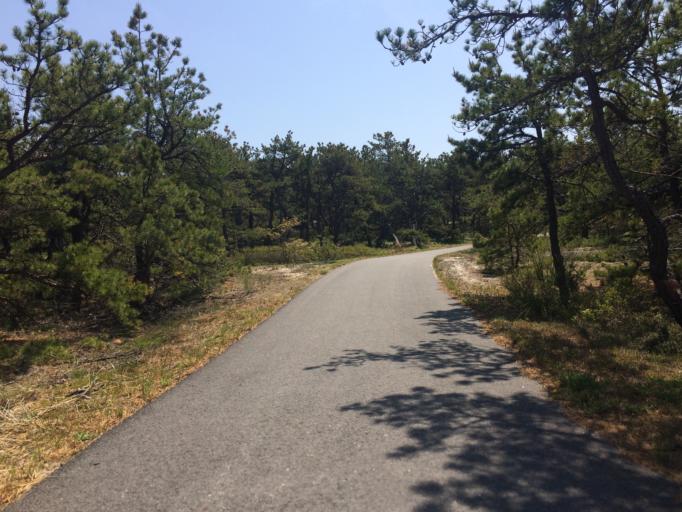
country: US
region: Massachusetts
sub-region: Barnstable County
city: Provincetown
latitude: 42.0747
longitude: -70.2108
